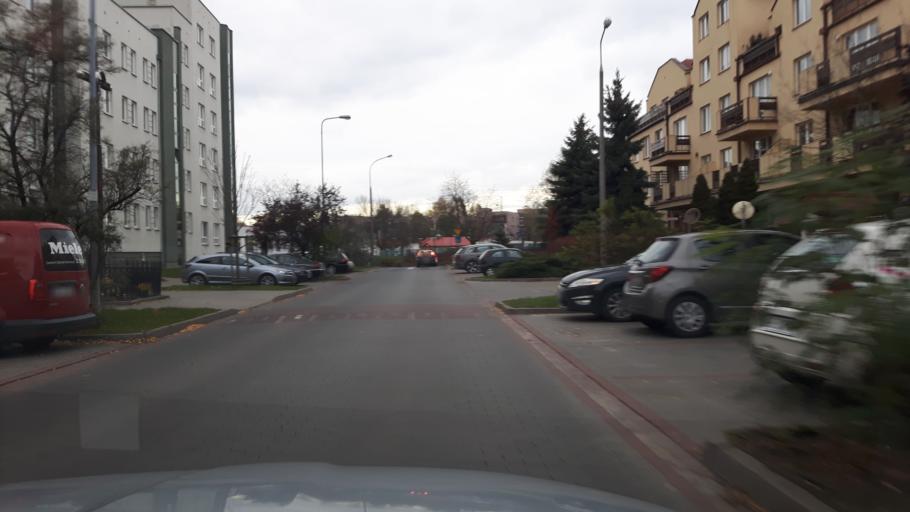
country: PL
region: Masovian Voivodeship
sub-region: Warszawa
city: Ursynow
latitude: 52.1554
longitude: 21.0553
